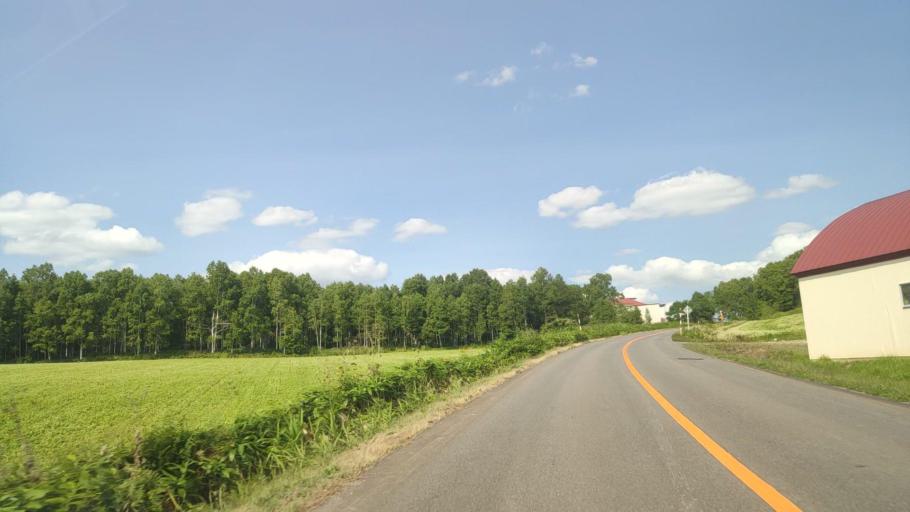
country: JP
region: Hokkaido
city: Nayoro
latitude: 44.2799
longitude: 142.4237
